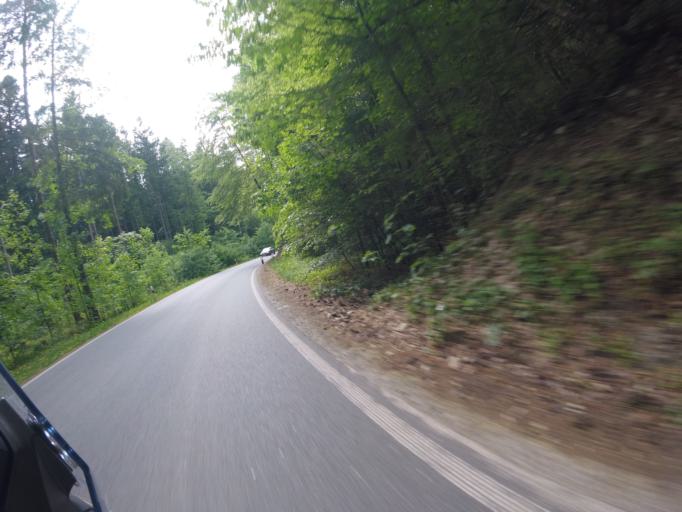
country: DE
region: Bavaria
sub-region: Upper Bavaria
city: Reichertshausen
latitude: 47.8776
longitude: 11.5318
